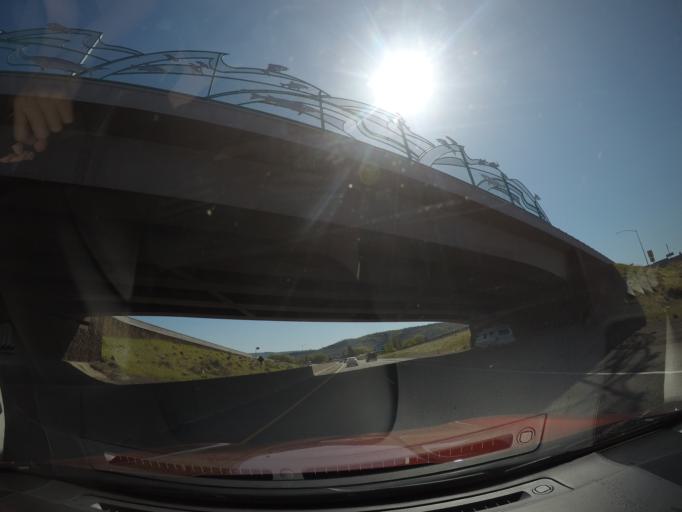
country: US
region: Oregon
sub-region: Wasco County
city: Chenoweth
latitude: 45.6309
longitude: -121.2134
